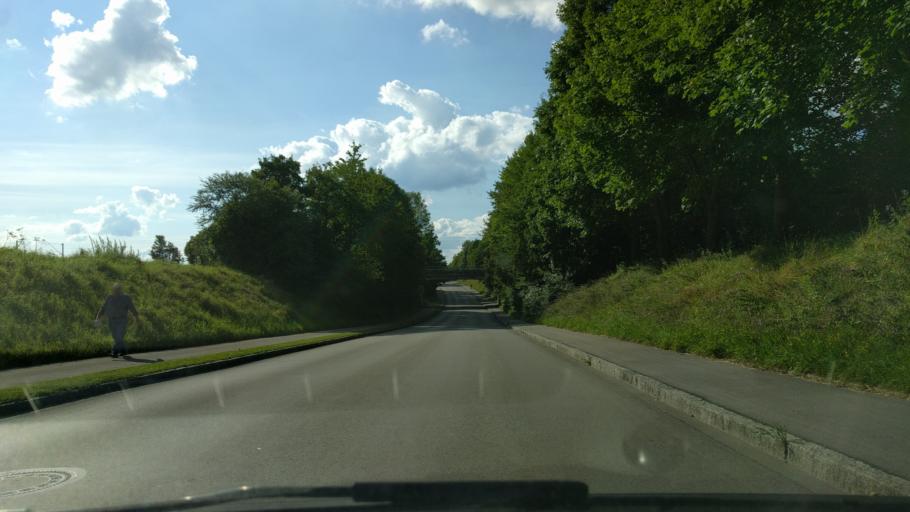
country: DE
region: Bavaria
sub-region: Upper Bavaria
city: Oberhaching
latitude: 48.0278
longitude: 11.5866
